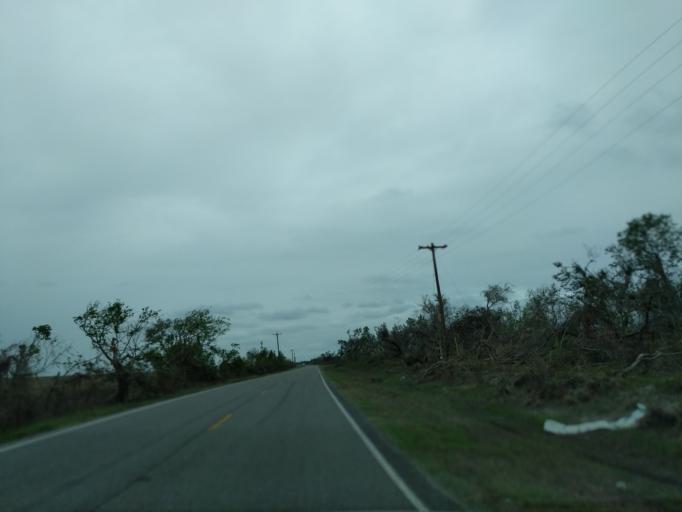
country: US
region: Louisiana
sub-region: Cameron Parish
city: Cameron
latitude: 29.7867
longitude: -93.1425
